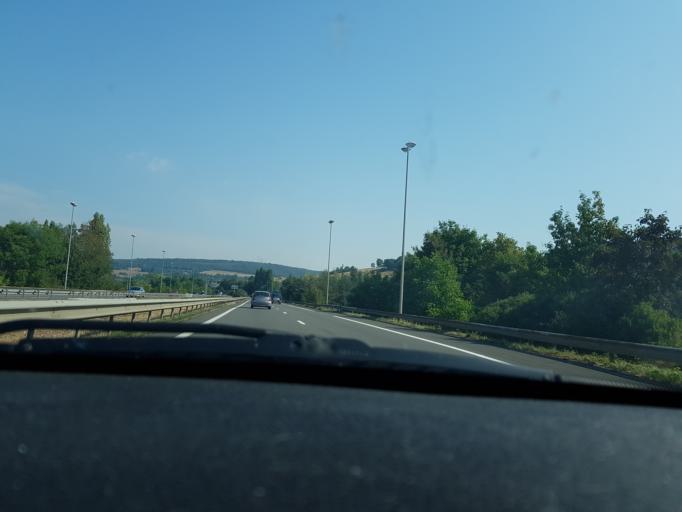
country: FR
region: Lorraine
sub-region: Departement de Meurthe-et-Moselle
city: Custines
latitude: 48.7755
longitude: 6.1443
